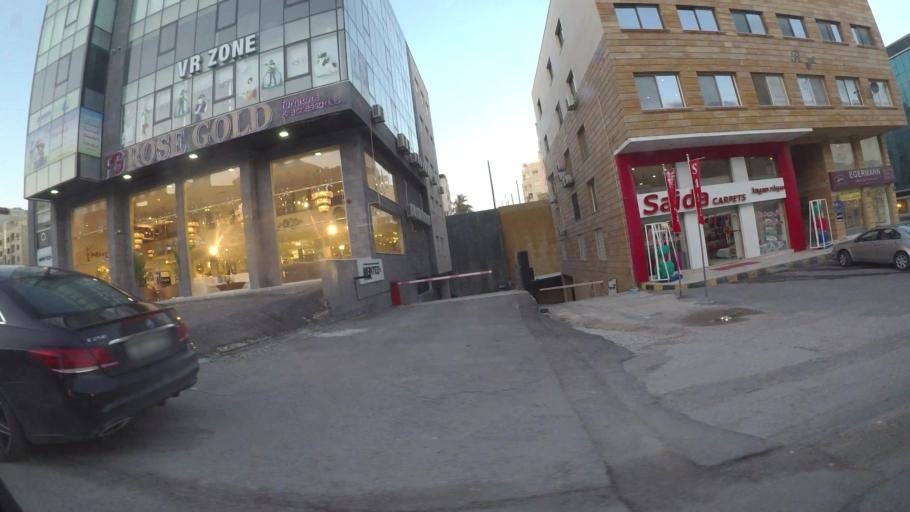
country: JO
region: Amman
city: Al Jubayhah
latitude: 31.9958
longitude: 35.8561
